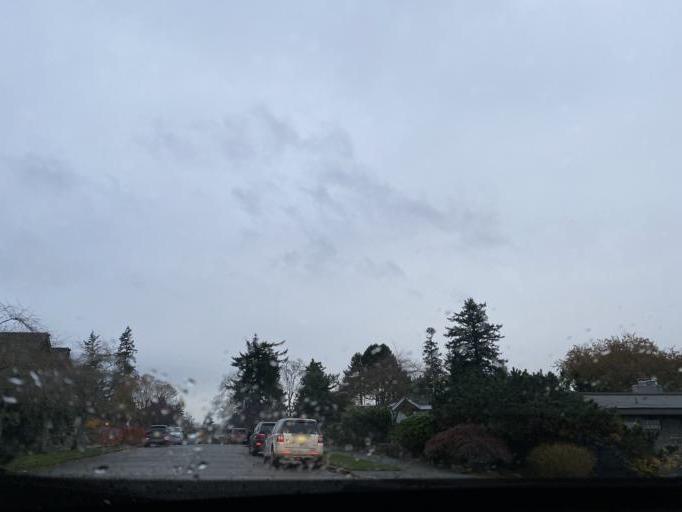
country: US
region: Washington
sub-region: King County
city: Seattle
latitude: 47.6487
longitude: -122.4131
